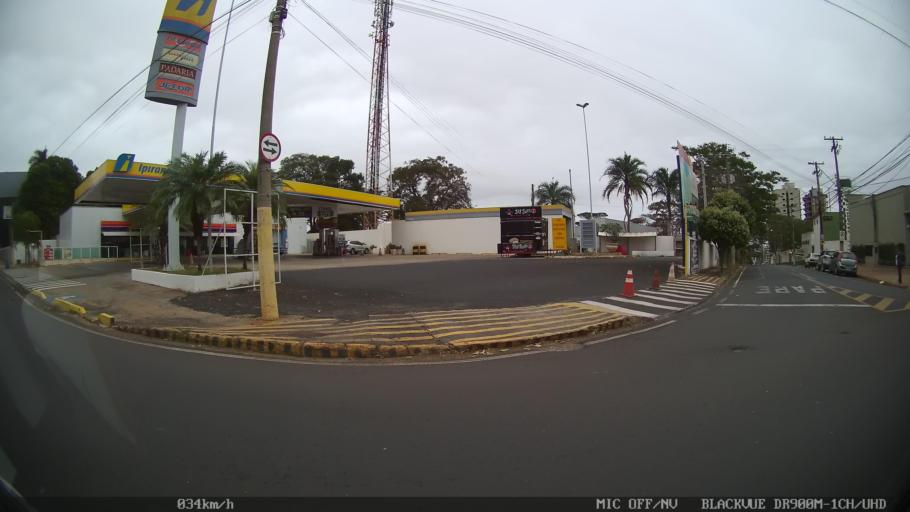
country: BR
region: Sao Paulo
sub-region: Sao Jose Do Rio Preto
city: Sao Jose do Rio Preto
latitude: -20.8359
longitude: -49.4005
